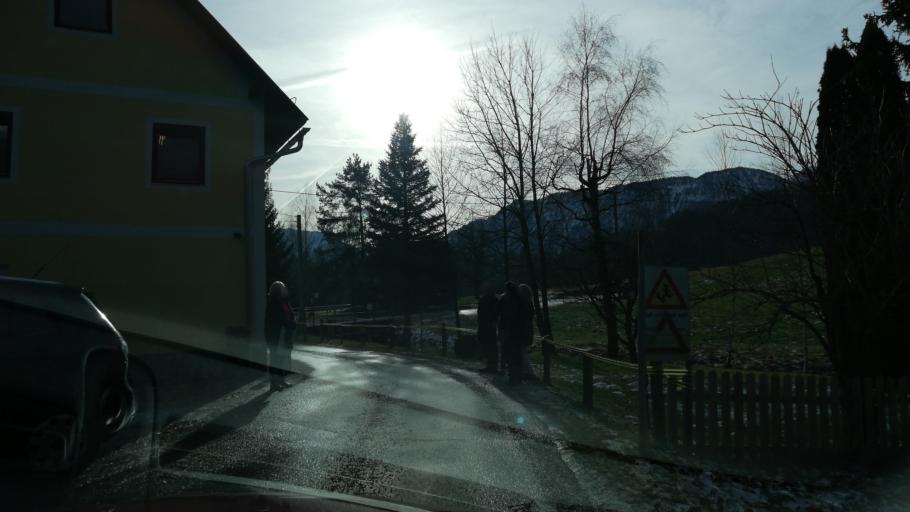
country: AT
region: Upper Austria
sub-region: Politischer Bezirk Kirchdorf an der Krems
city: Rossleithen
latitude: 47.7155
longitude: 14.3488
